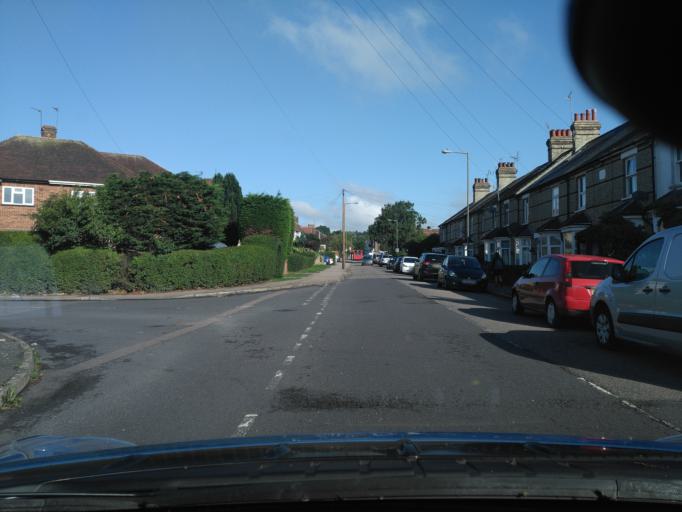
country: GB
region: England
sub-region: Greater London
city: High Barnet
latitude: 51.6451
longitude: -0.2131
